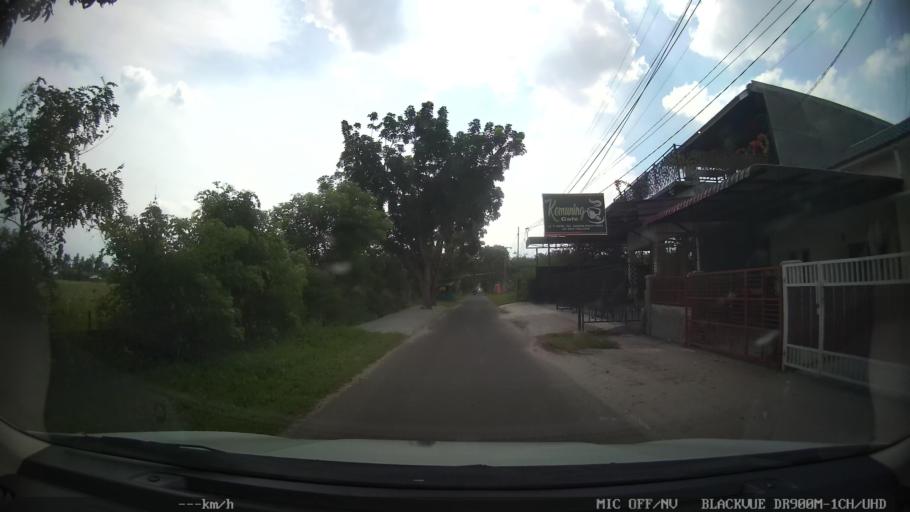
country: ID
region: North Sumatra
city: Binjai
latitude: 3.6205
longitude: 98.5130
